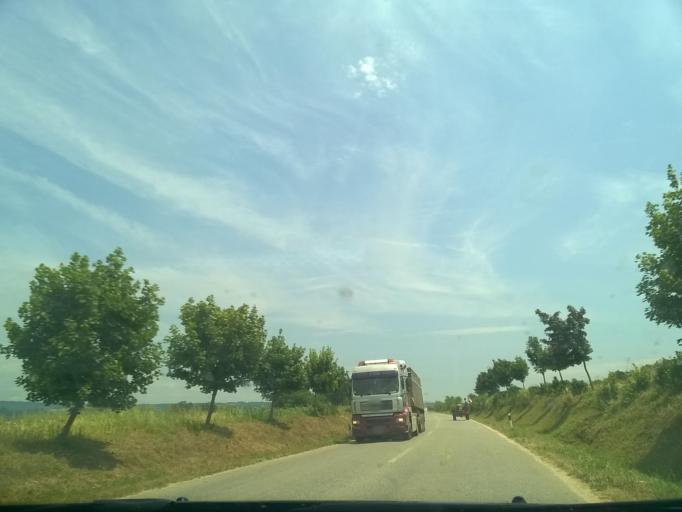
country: RS
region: Central Serbia
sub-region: Zajecarski Okrug
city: Soko Banja
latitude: 43.6560
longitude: 21.8205
